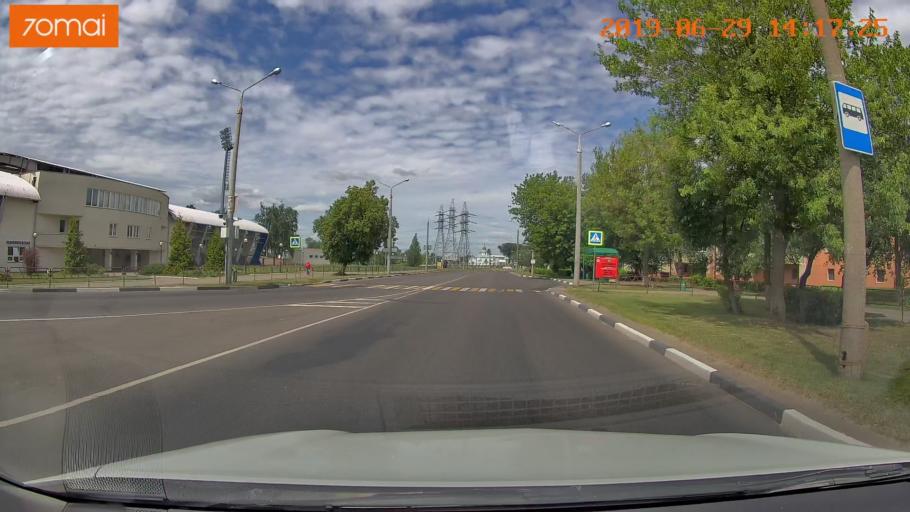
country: BY
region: Minsk
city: Salihorsk
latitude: 52.7984
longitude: 27.5396
